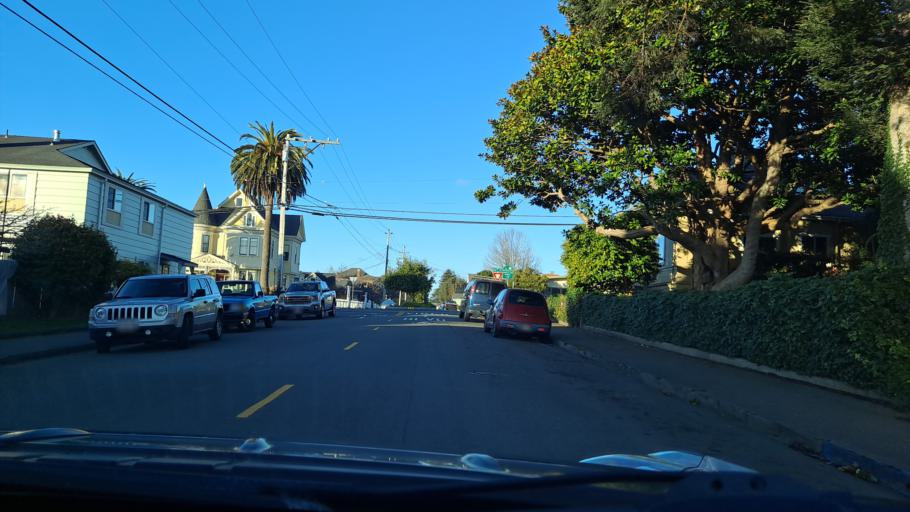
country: US
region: California
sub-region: Humboldt County
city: Arcata
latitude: 40.8728
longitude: -124.0865
